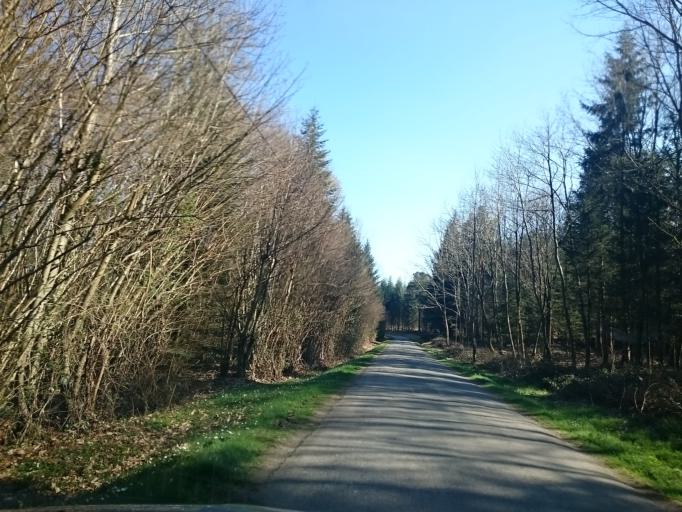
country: FR
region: Brittany
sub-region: Departement d'Ille-et-Vilaine
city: Crevin
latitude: 47.9612
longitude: -1.6726
